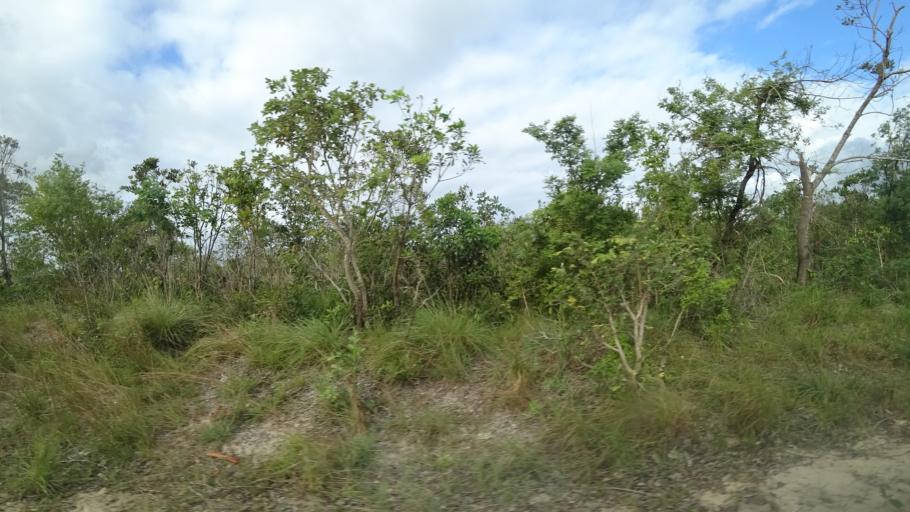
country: MZ
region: Sofala
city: Beira
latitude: -19.6405
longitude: 35.0593
